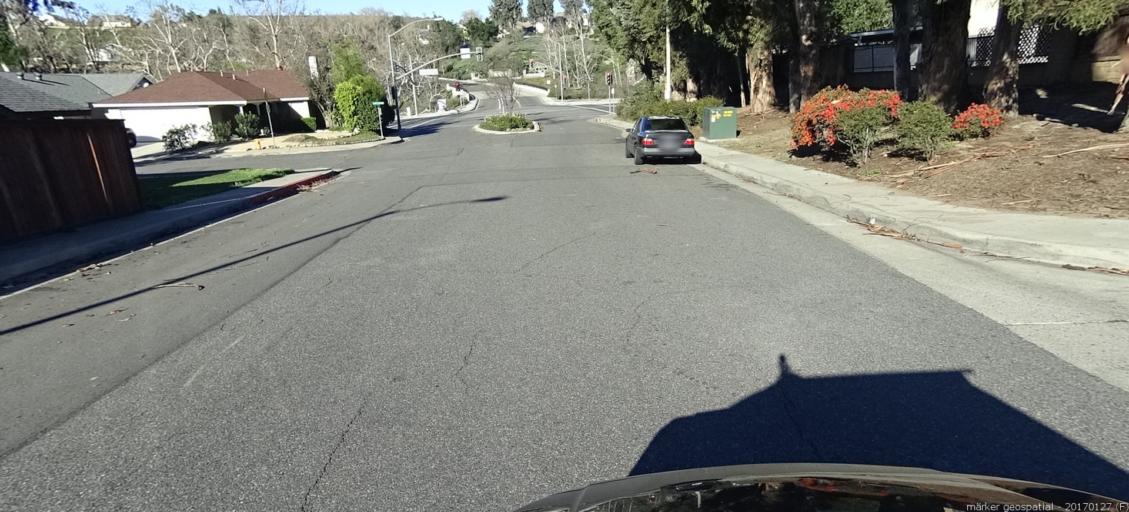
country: US
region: California
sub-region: Orange County
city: Lake Forest
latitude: 33.6542
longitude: -117.6580
